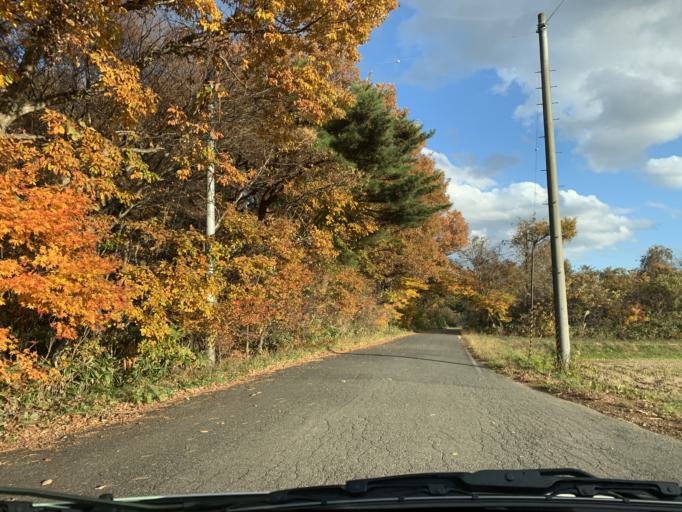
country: JP
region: Iwate
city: Mizusawa
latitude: 39.1209
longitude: 140.9920
